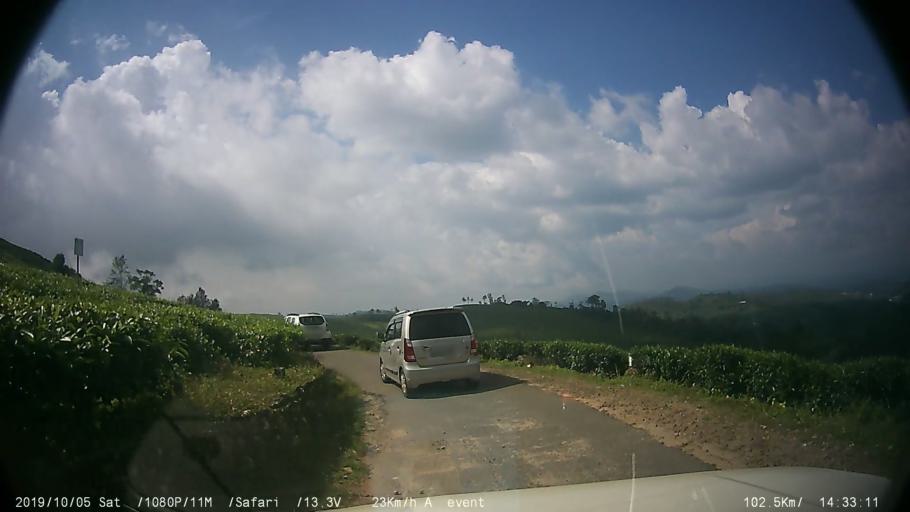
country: IN
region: Kerala
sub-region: Kottayam
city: Erattupetta
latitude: 9.6145
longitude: 76.9674
